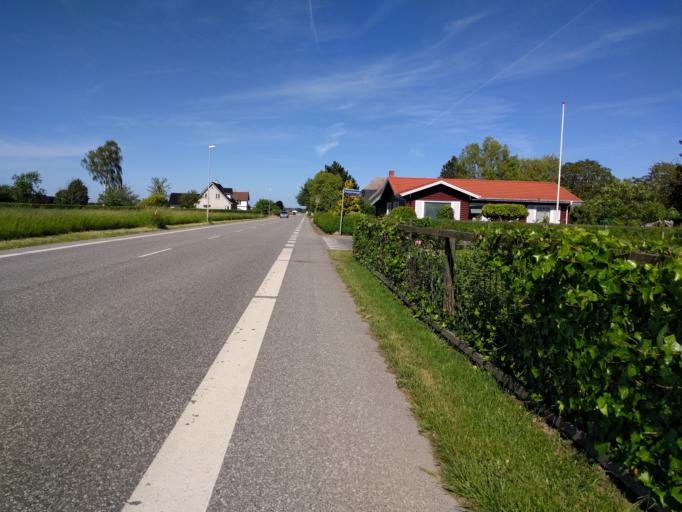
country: DK
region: South Denmark
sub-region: Kerteminde Kommune
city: Kerteminde
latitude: 55.4115
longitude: 10.6289
